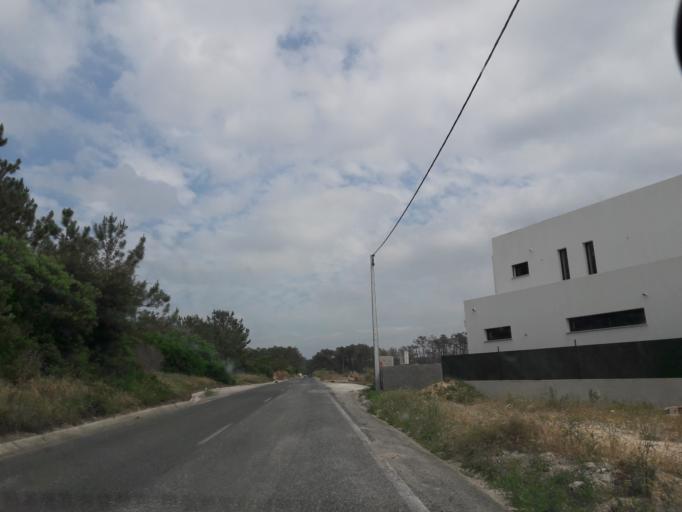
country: PT
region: Leiria
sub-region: Peniche
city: Atouguia da Baleia
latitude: 39.3598
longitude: -9.3050
